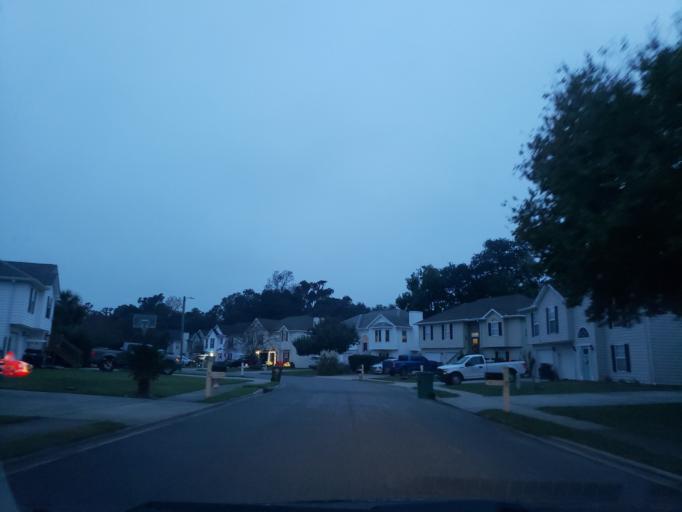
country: US
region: Georgia
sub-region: Chatham County
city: Wilmington Island
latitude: 32.0237
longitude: -80.9582
